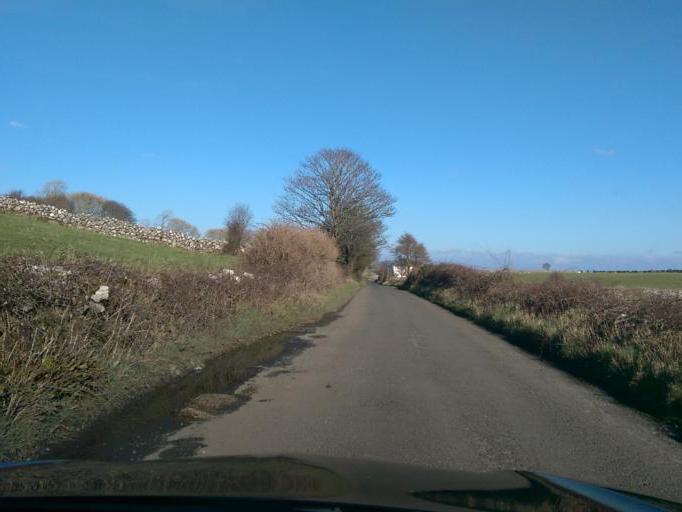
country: IE
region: Connaught
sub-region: County Galway
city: Oranmore
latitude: 53.2240
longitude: -8.9326
